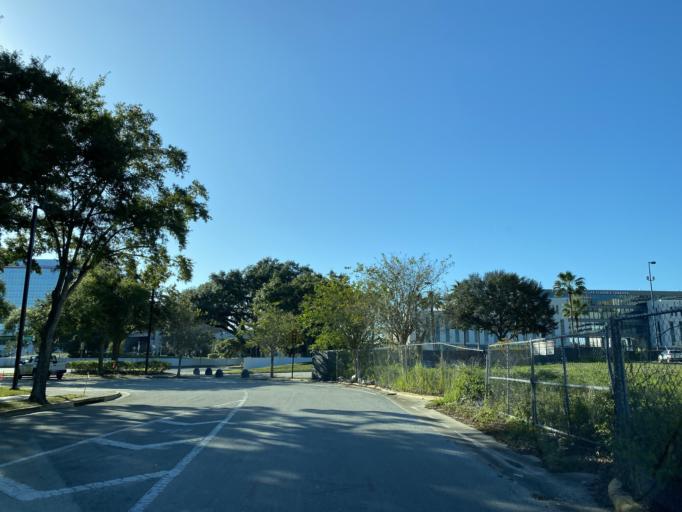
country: US
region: Florida
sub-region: Orange County
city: Orlando
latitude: 28.5489
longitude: -81.3856
